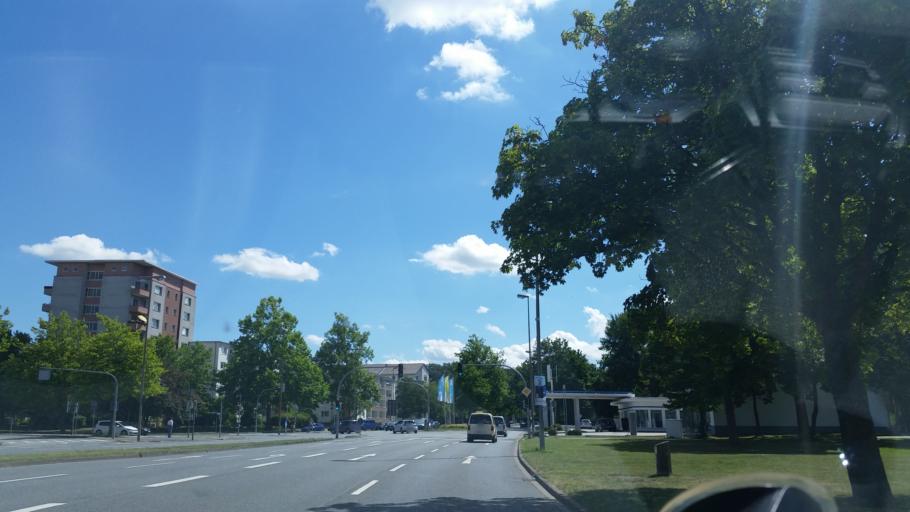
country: DE
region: Lower Saxony
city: Wolfsburg
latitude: 52.4176
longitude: 10.7835
